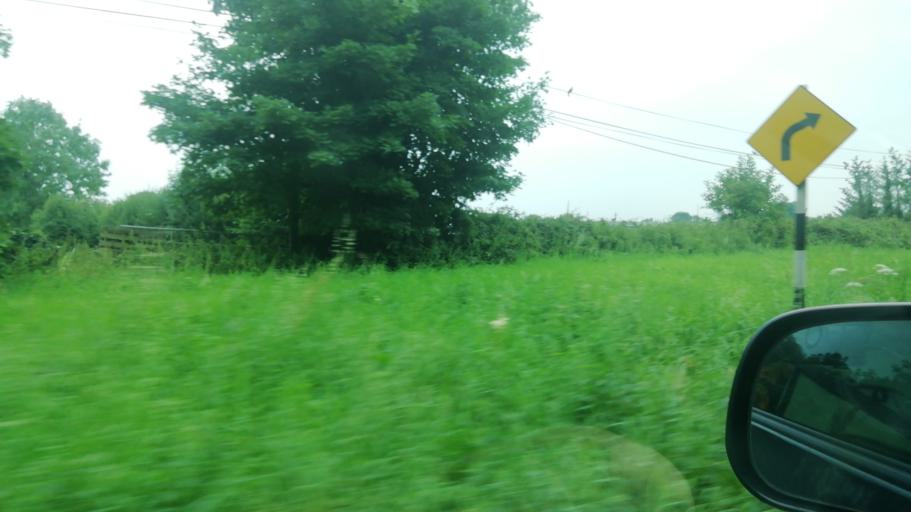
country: IE
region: Munster
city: Fethard
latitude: 52.5316
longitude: -7.6795
